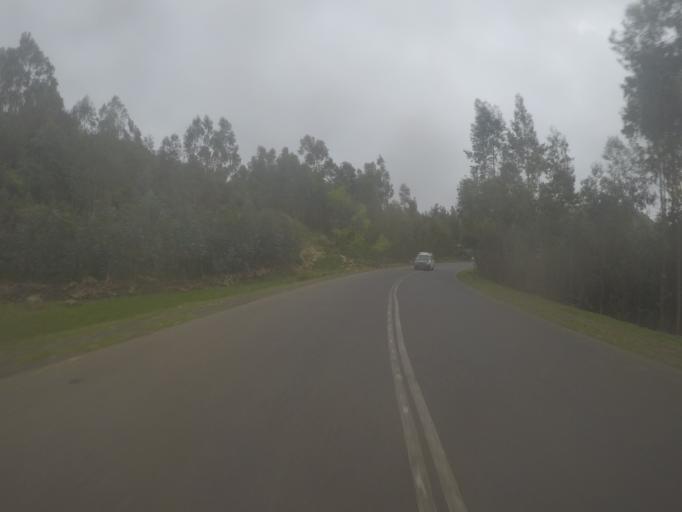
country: ET
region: Amhara
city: Gondar
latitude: 12.7388
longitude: 37.5145
